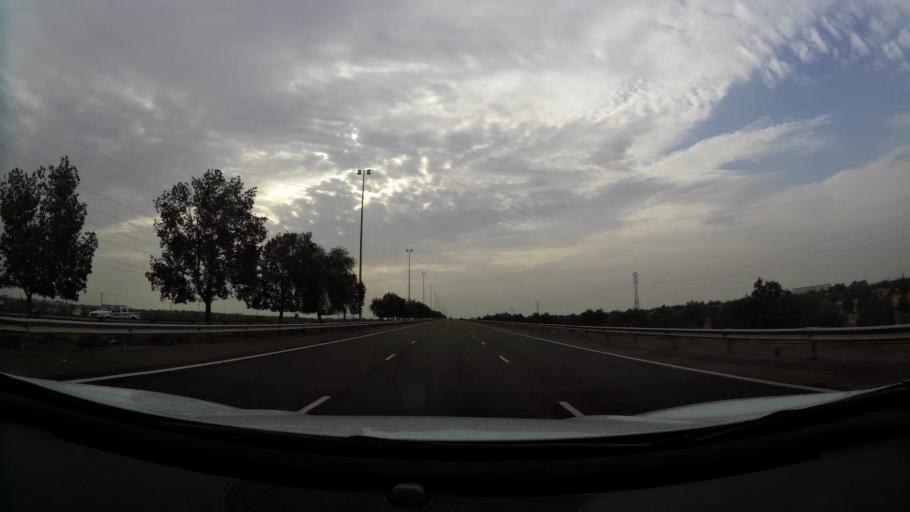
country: AE
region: Abu Dhabi
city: Abu Dhabi
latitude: 24.2113
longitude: 54.8903
